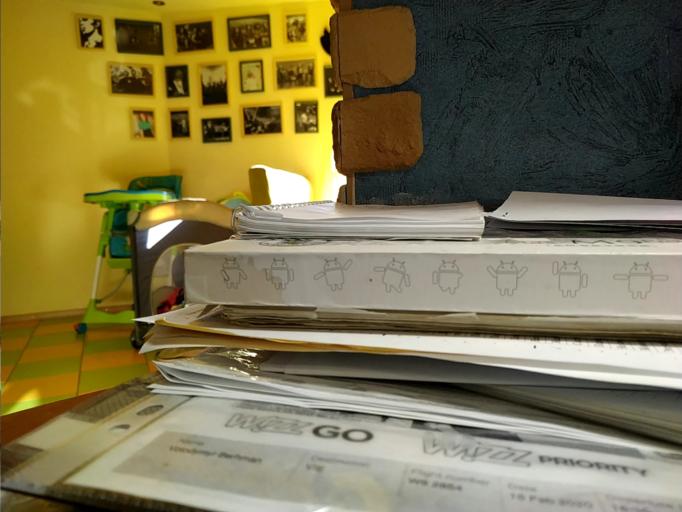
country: RU
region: Novgorod
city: Volot
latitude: 57.6230
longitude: 30.7748
